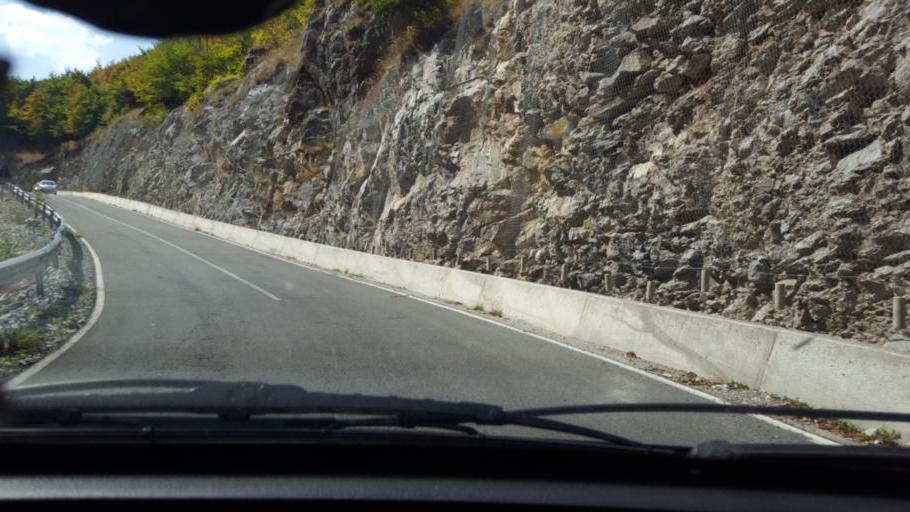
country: ME
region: Andrijevica
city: Andrijevica
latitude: 42.5623
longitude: 19.7324
